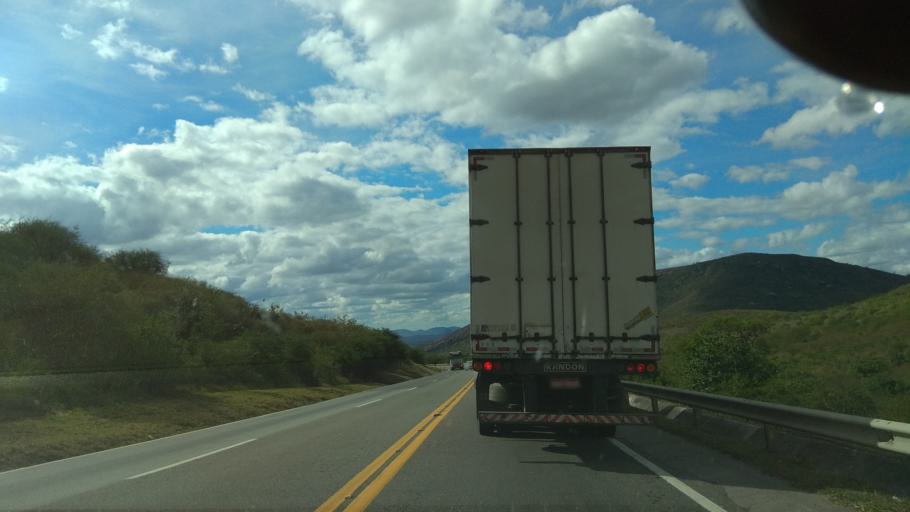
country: BR
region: Bahia
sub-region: Amargosa
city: Amargosa
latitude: -12.8913
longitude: -39.8594
